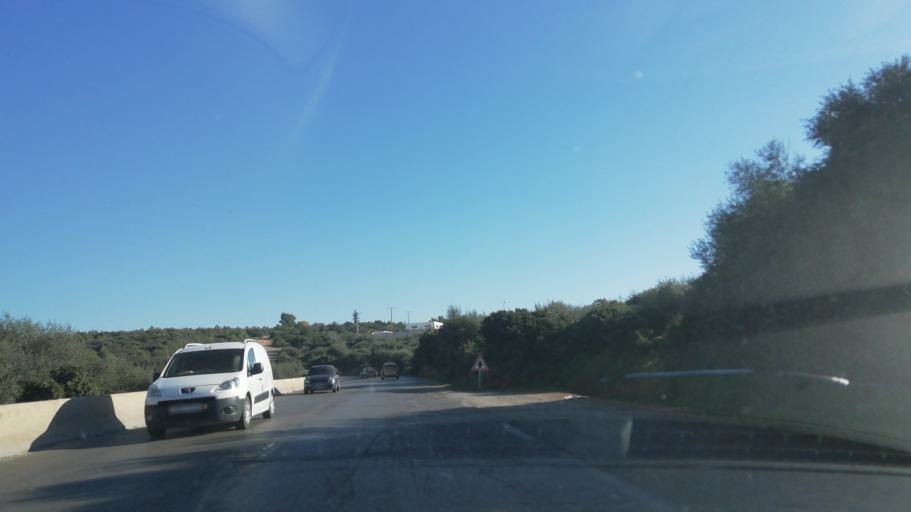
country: DZ
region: Relizane
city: Smala
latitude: 35.7011
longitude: 0.7725
